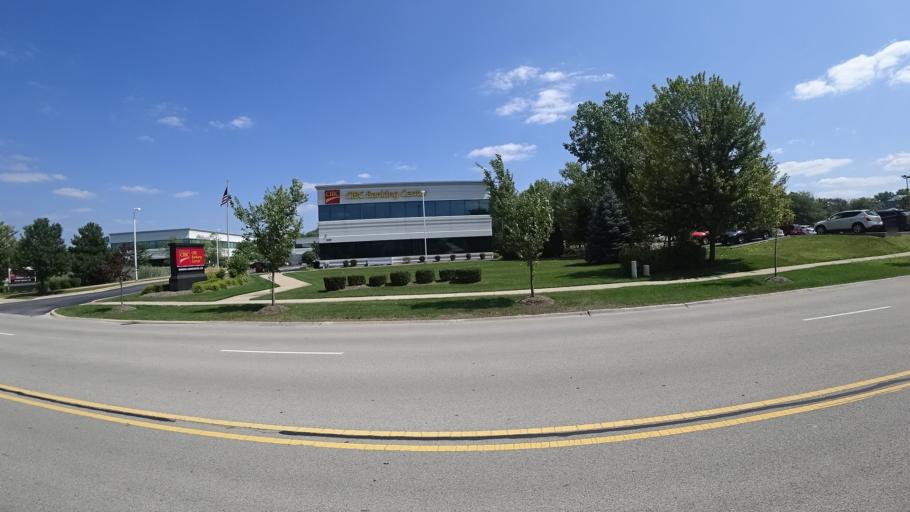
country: US
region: Illinois
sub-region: Cook County
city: Orland Park
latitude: 41.6262
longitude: -87.8511
